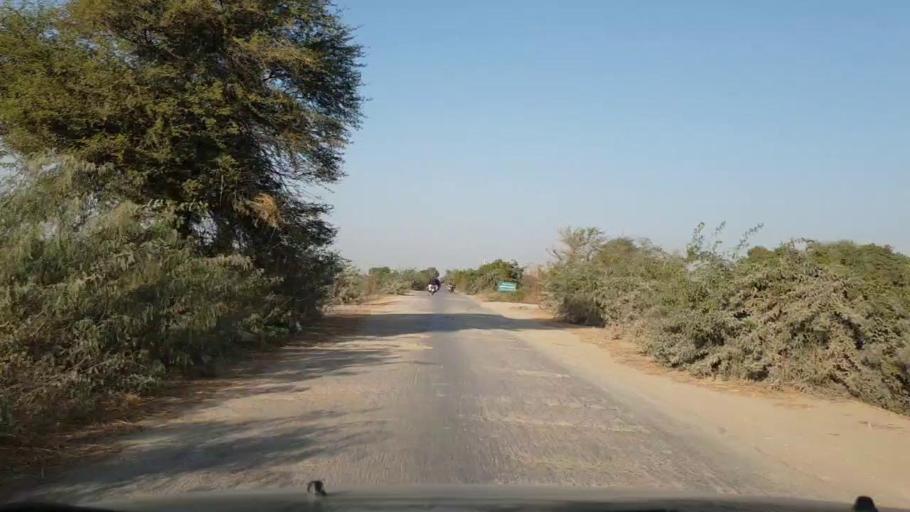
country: PK
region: Sindh
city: Chambar
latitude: 25.2370
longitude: 68.7851
